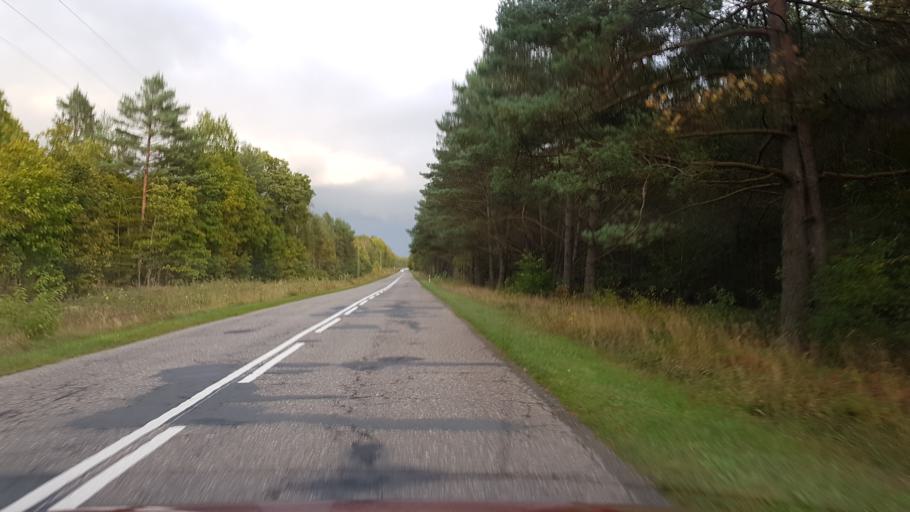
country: PL
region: West Pomeranian Voivodeship
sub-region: Powiat walecki
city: Tuczno
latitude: 53.1720
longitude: 16.3111
